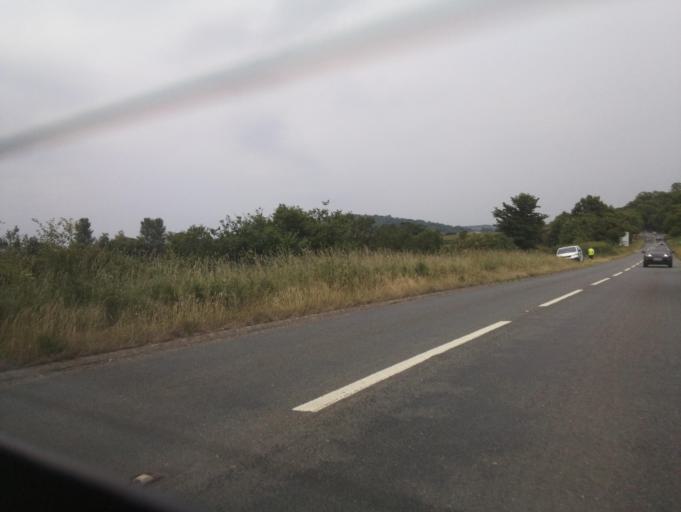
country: GB
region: England
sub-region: Devon
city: Colyton
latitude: 50.7288
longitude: -3.0494
